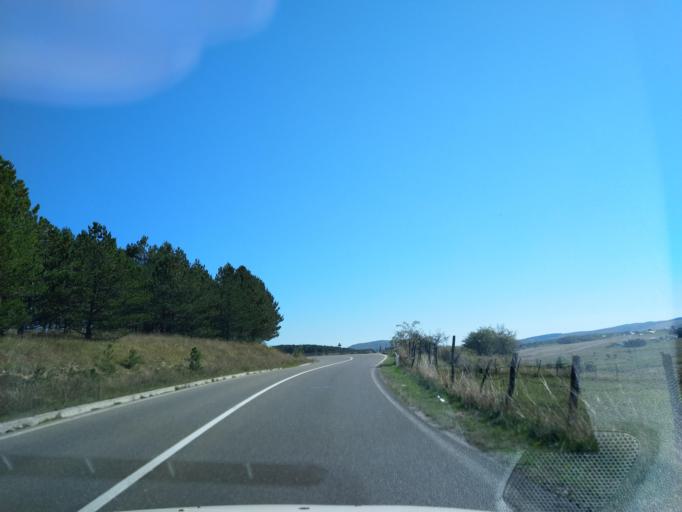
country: RS
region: Central Serbia
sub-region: Zlatiborski Okrug
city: Sjenica
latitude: 43.2672
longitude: 20.0358
